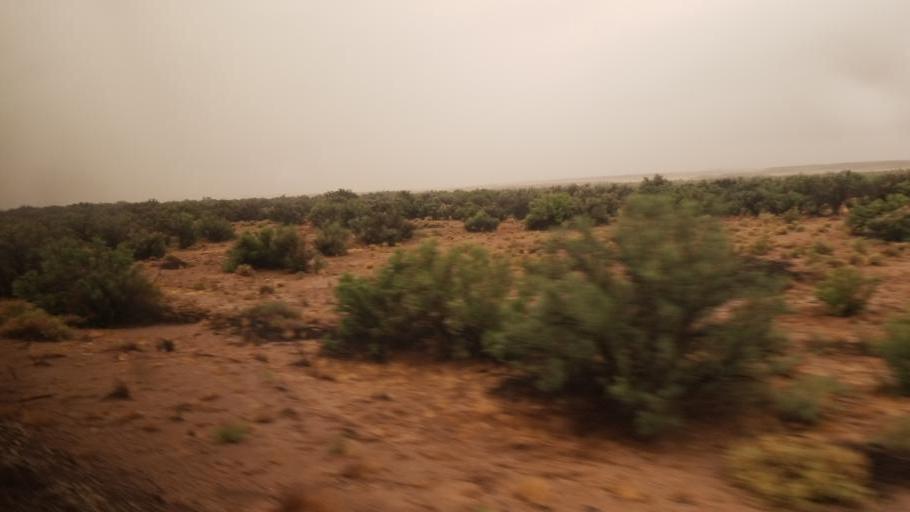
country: US
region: Arizona
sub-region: Navajo County
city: Joseph City
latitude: 34.9563
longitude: -110.3651
